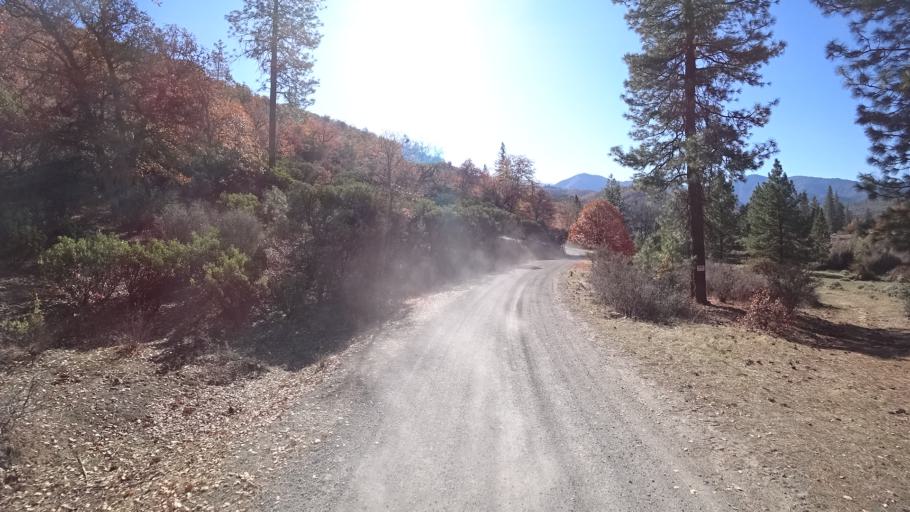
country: US
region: California
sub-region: Siskiyou County
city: Yreka
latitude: 41.8417
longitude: -122.8361
